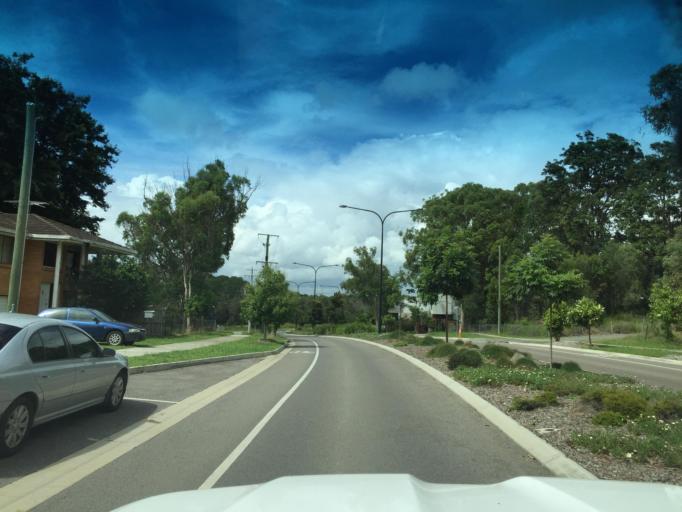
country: AU
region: Queensland
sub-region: Moreton Bay
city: Mango Hill
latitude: -27.2289
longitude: 153.0290
